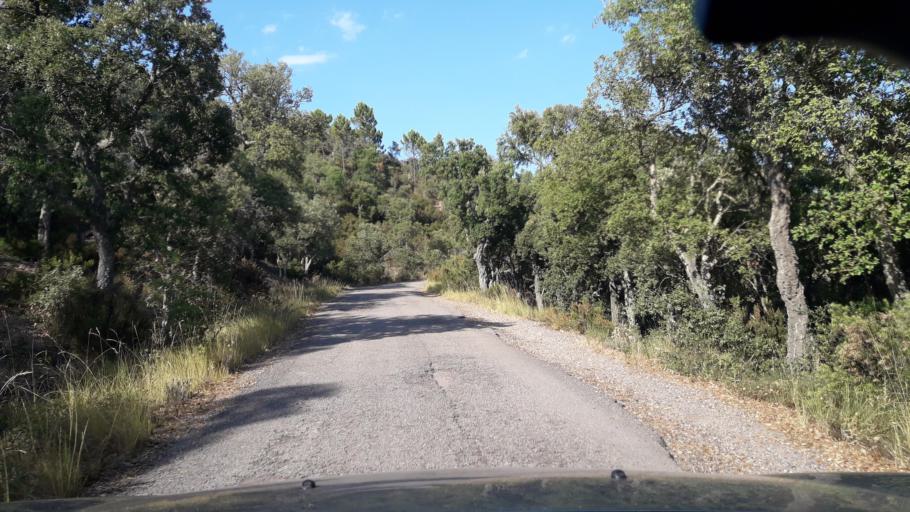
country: FR
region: Provence-Alpes-Cote d'Azur
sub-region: Departement du Var
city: Saint-Raphael
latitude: 43.4962
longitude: 6.8026
